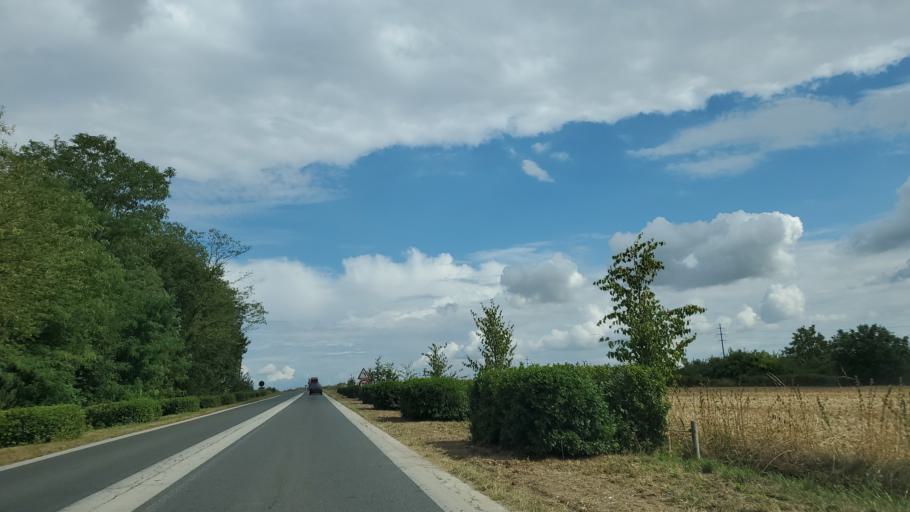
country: FR
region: Ile-de-France
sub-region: Departement de Seine-et-Marne
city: Chailly-en-Brie
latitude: 48.7883
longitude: 3.1283
